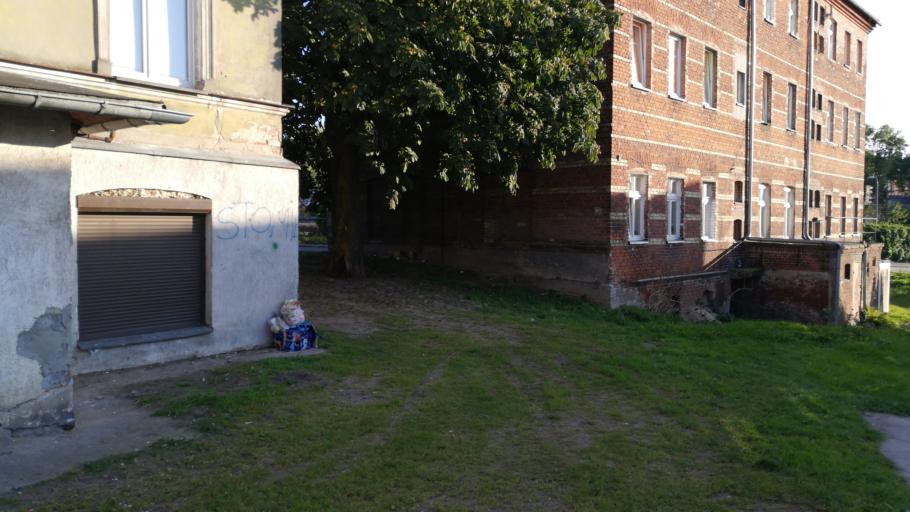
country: PL
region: Warmian-Masurian Voivodeship
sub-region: Powiat olsztynski
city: Olsztyn
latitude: 53.7849
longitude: 20.4907
